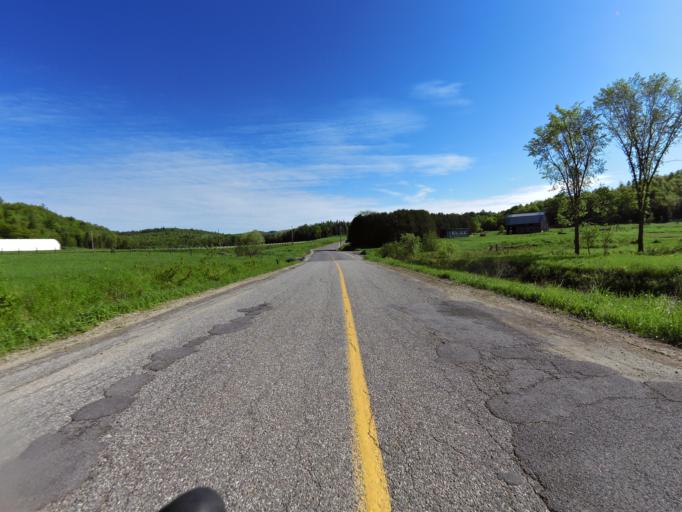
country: CA
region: Quebec
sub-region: Outaouais
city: Wakefield
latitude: 45.6426
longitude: -75.8909
